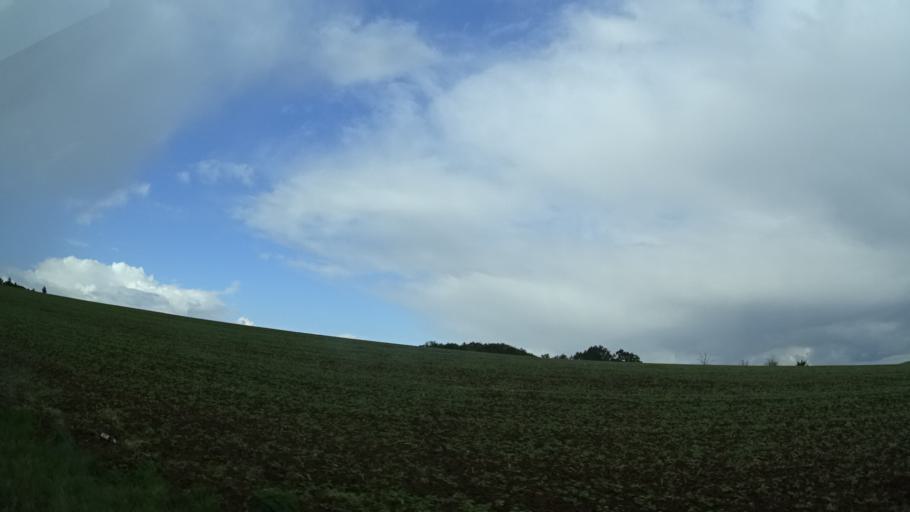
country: DE
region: Bavaria
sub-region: Regierungsbezirk Unterfranken
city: Kleinrinderfeld
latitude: 49.6855
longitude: 9.8218
